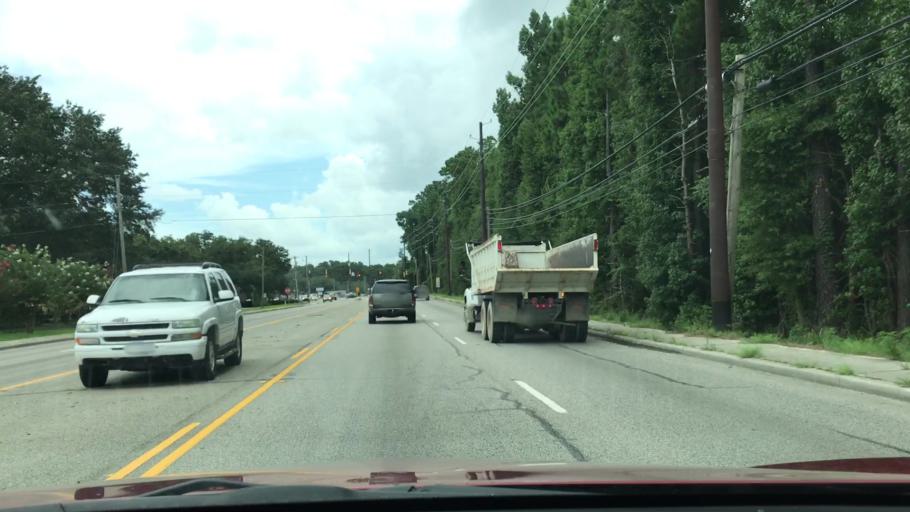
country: US
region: South Carolina
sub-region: Georgetown County
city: Georgetown
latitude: 33.4022
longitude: -79.2888
